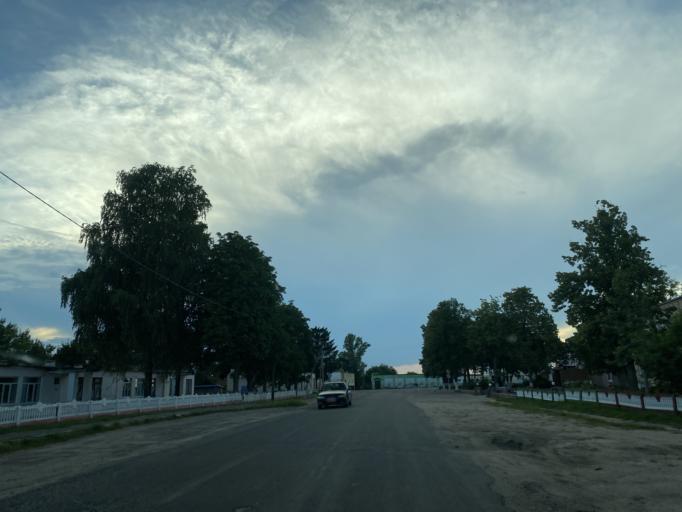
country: BY
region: Brest
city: Ivanava
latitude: 52.2358
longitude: 25.6699
